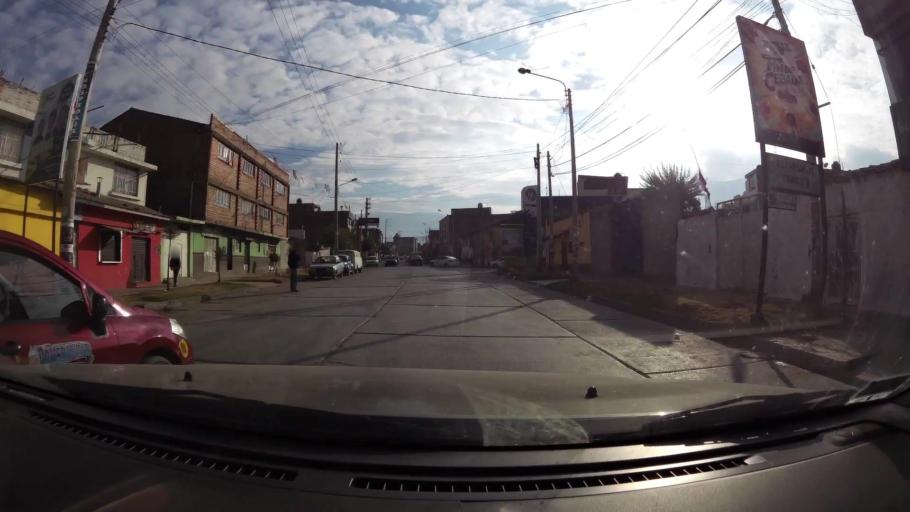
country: PE
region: Junin
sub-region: Provincia de Huancayo
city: Huancayo
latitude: -12.0573
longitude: -75.2052
